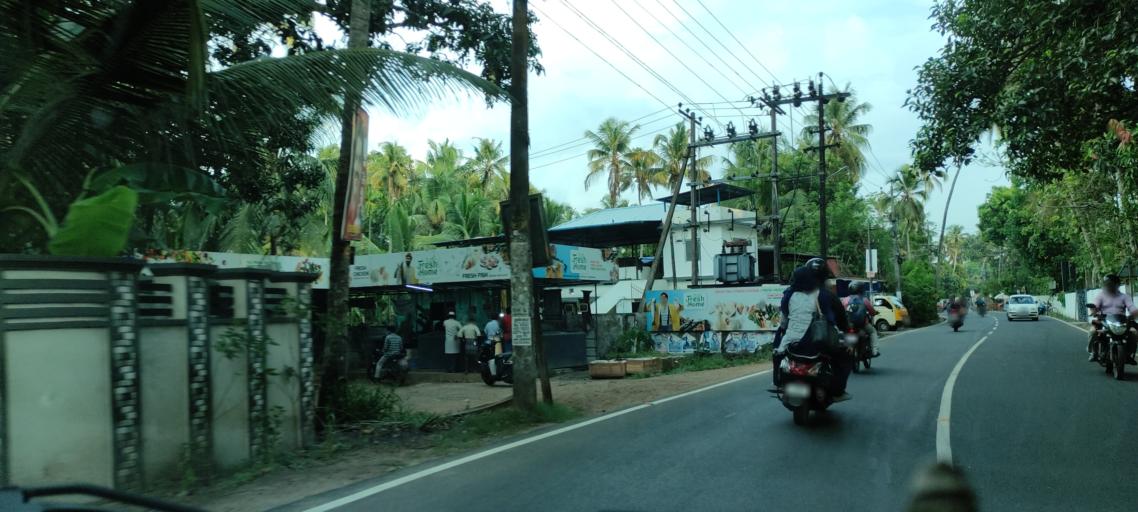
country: IN
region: Kerala
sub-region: Alappuzha
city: Arukutti
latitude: 9.8610
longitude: 76.3245
